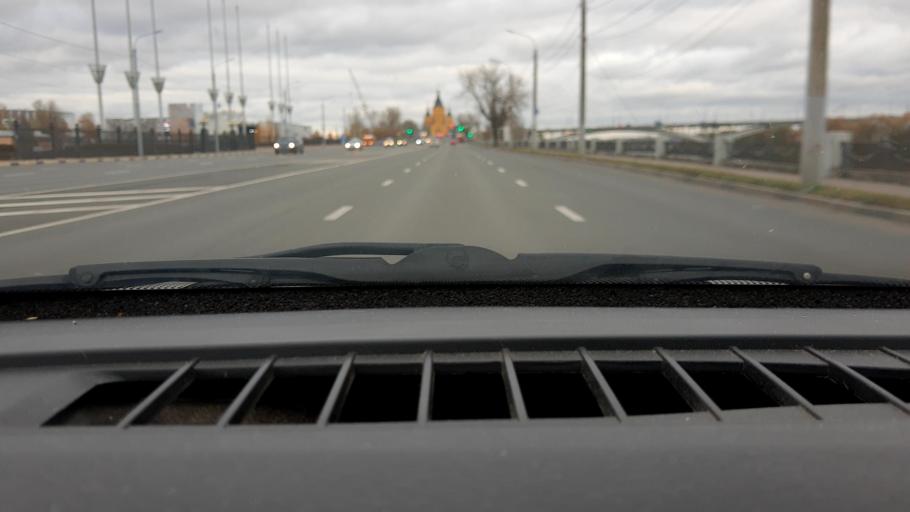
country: RU
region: Nizjnij Novgorod
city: Nizhniy Novgorod
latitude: 56.3224
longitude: 43.9635
